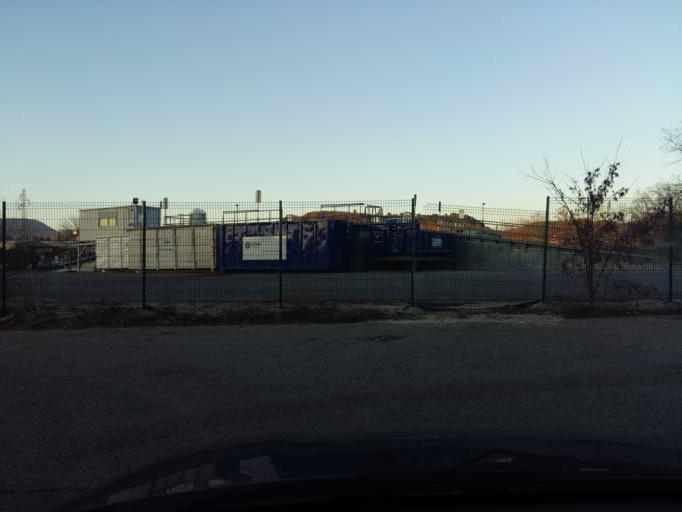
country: FR
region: Rhone-Alpes
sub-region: Departement de la Drome
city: La Garde-Adhemar
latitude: 44.4157
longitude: 4.8065
